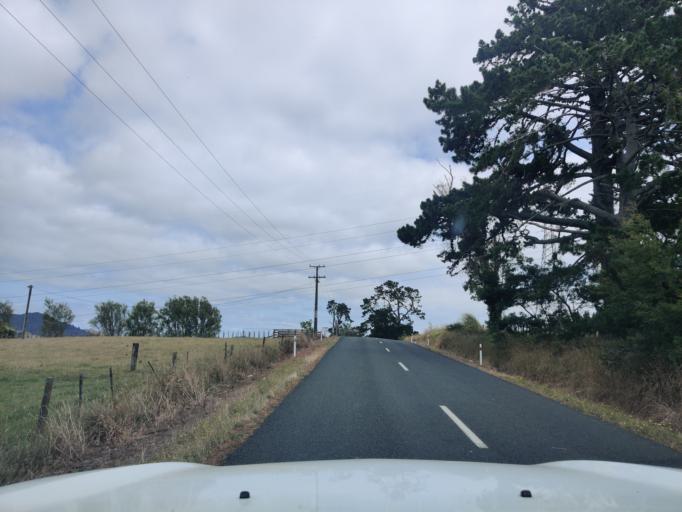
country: NZ
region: Waikato
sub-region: Waikato District
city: Te Kauwhata
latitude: -37.5155
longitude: 175.1761
